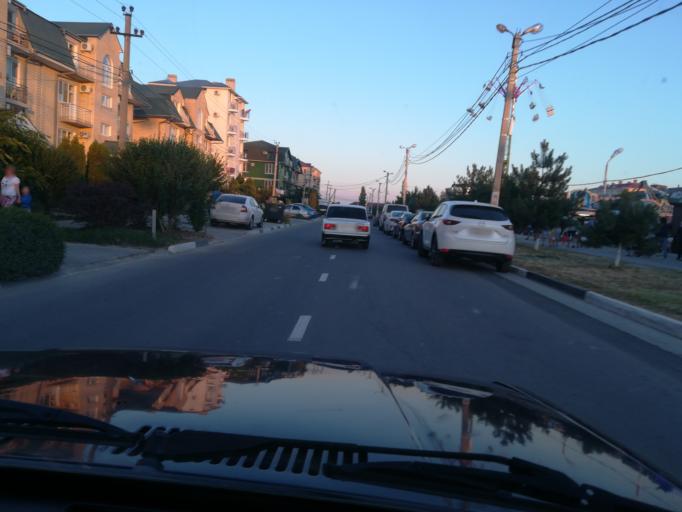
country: RU
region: Krasnodarskiy
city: Vityazevo
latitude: 44.9869
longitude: 37.2584
